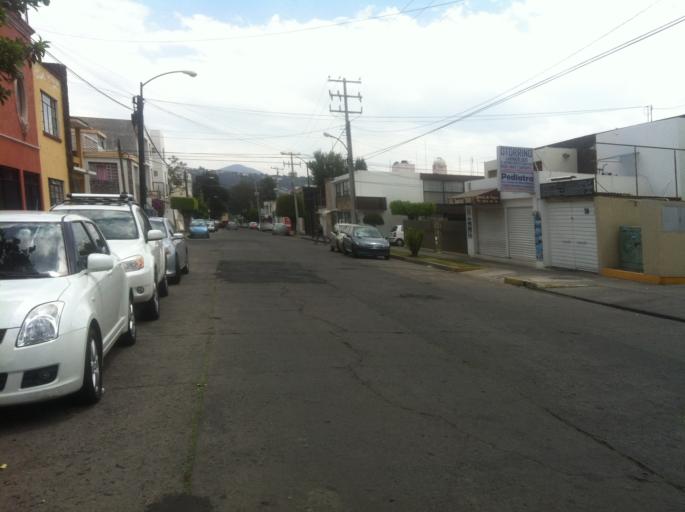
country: MX
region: Michoacan
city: Morelia
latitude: 19.6973
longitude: -101.1734
